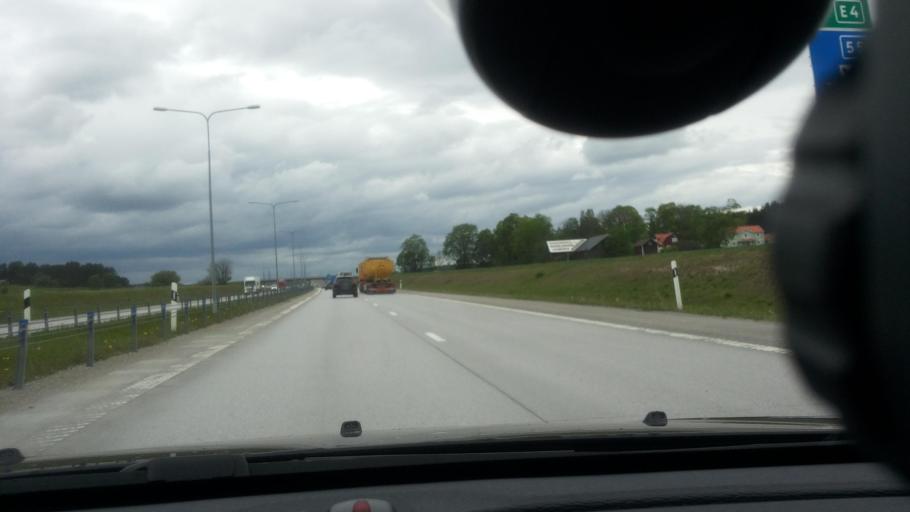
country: SE
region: Uppsala
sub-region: Uppsala Kommun
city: Saevja
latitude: 59.8763
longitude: 17.6960
